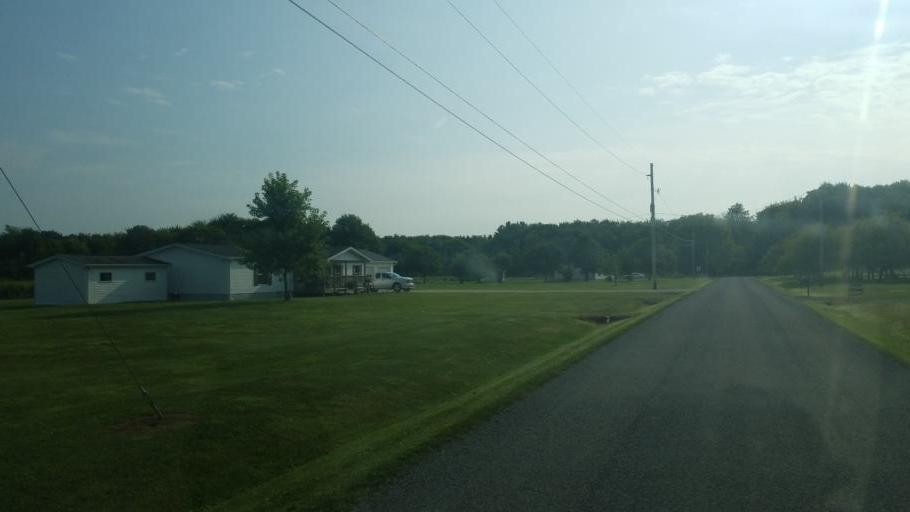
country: US
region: Pennsylvania
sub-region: Crawford County
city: Pymatuning Central
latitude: 41.6264
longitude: -80.4821
